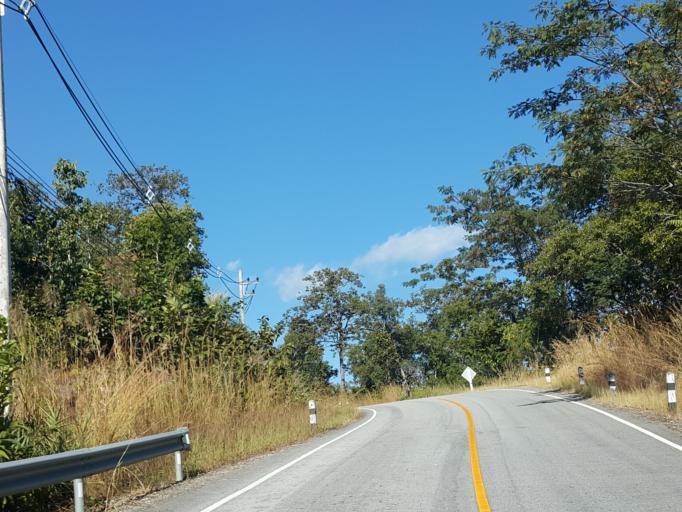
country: TH
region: Chiang Mai
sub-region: Amphoe Chiang Dao
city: Chiang Dao
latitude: 19.5262
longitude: 98.8864
